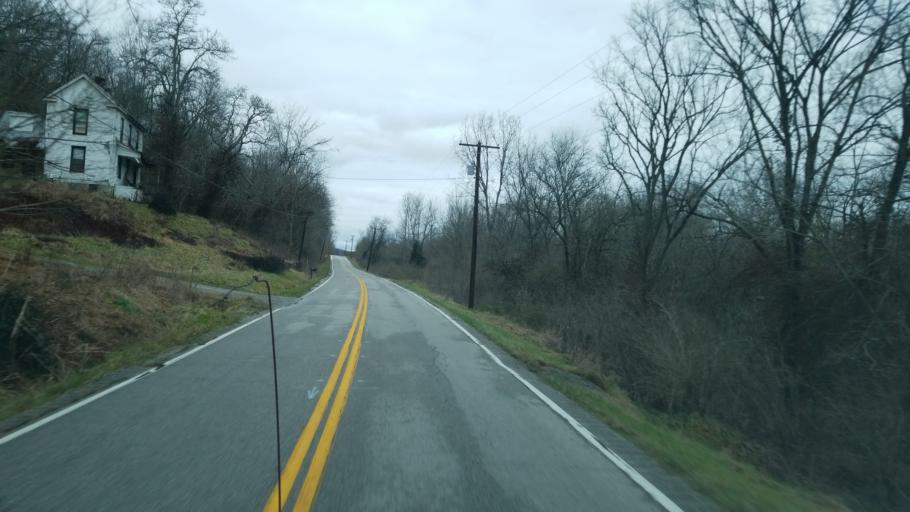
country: US
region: Ohio
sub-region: Clermont County
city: New Richmond
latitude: 38.9198
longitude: -84.2681
